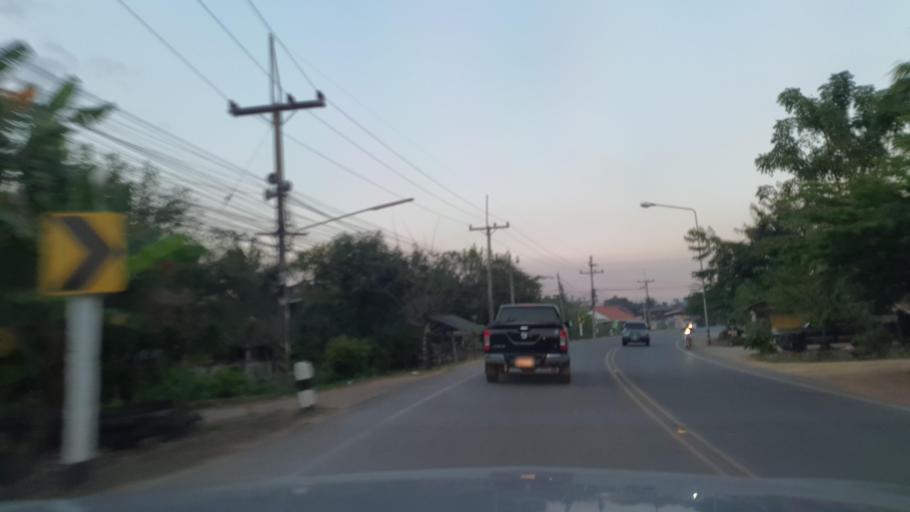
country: TH
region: Phayao
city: Dok Kham Tai
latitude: 19.0850
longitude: 100.0627
